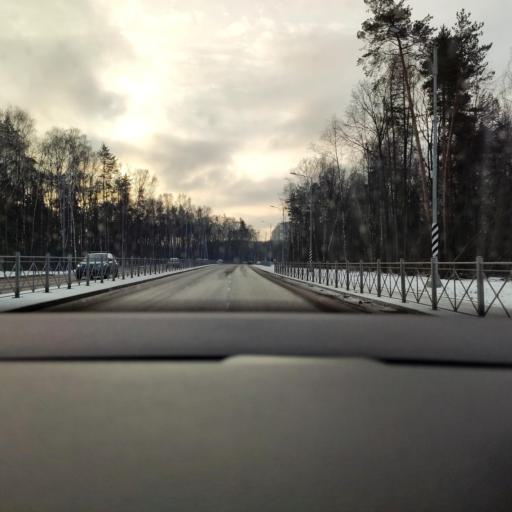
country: RU
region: Moskovskaya
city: Reutov
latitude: 55.7646
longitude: 37.8825
